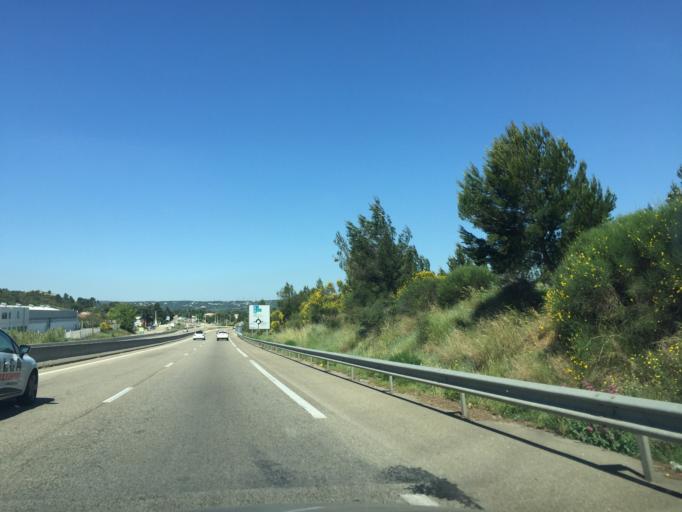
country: FR
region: Languedoc-Roussillon
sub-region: Departement du Gard
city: Les Angles
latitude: 43.9581
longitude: 4.7387
